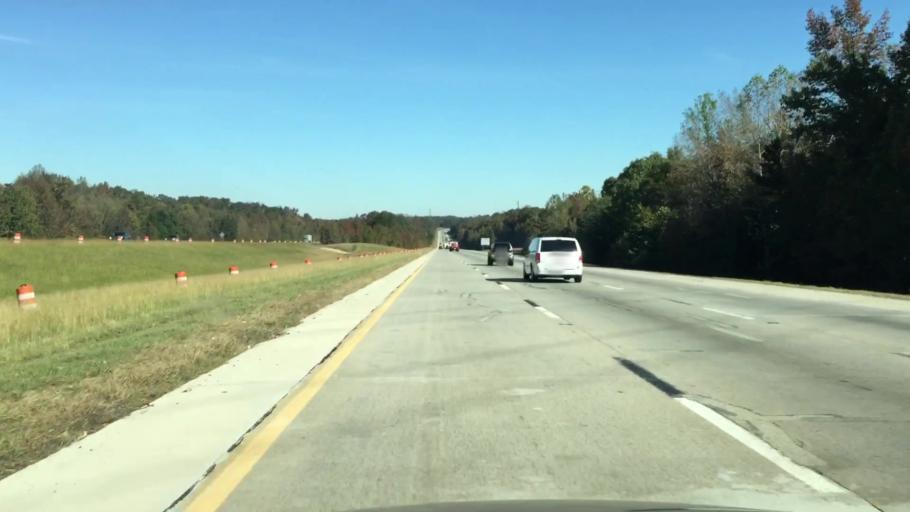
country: US
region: North Carolina
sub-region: Guilford County
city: Jamestown
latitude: 35.9639
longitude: -79.8934
